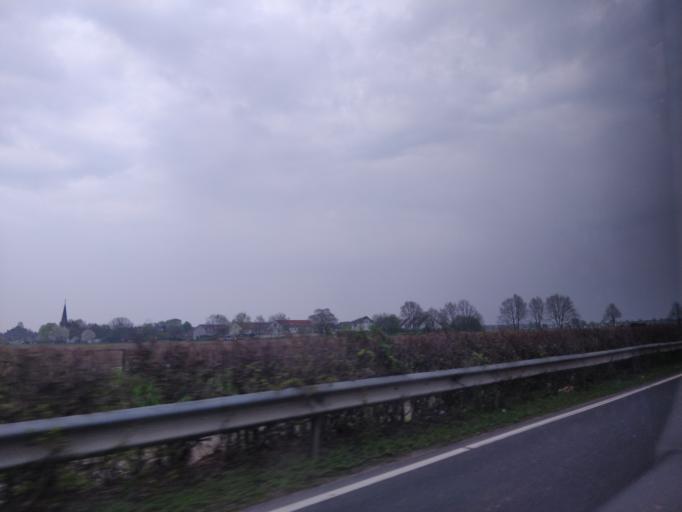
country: DE
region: North Rhine-Westphalia
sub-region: Regierungsbezirk Koln
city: Pulheim
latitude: 50.9633
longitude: 6.8192
